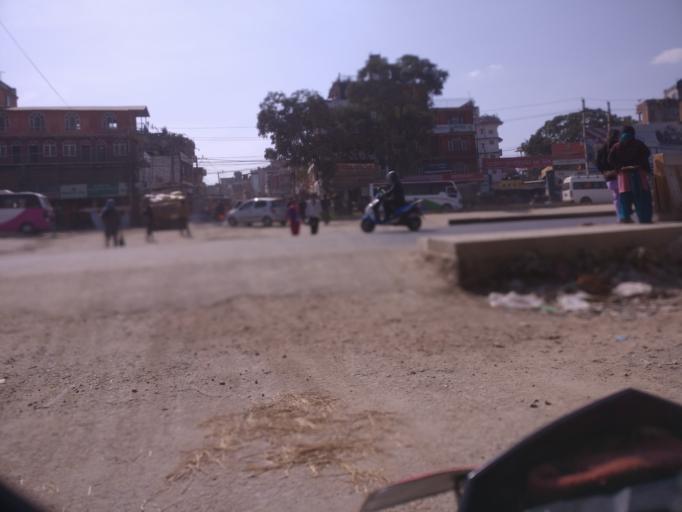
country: NP
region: Central Region
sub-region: Bagmati Zone
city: Patan
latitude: 27.6583
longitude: 85.3227
